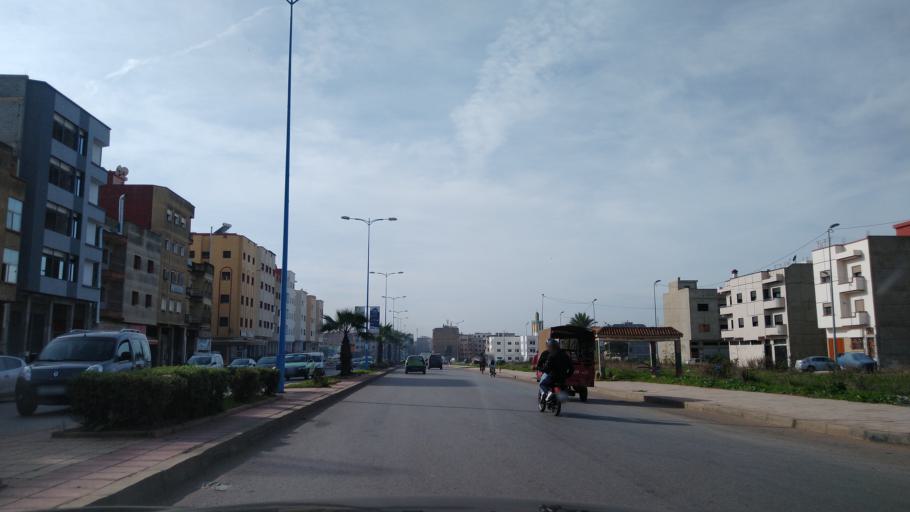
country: MA
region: Grand Casablanca
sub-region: Mohammedia
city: Mohammedia
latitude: 33.6831
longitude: -7.3816
